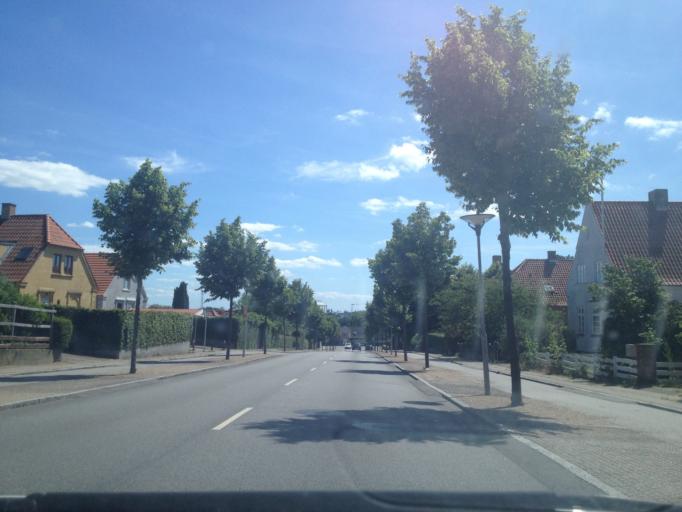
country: DK
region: Zealand
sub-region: Kalundborg Kommune
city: Kalundborg
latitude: 55.6826
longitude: 11.0995
